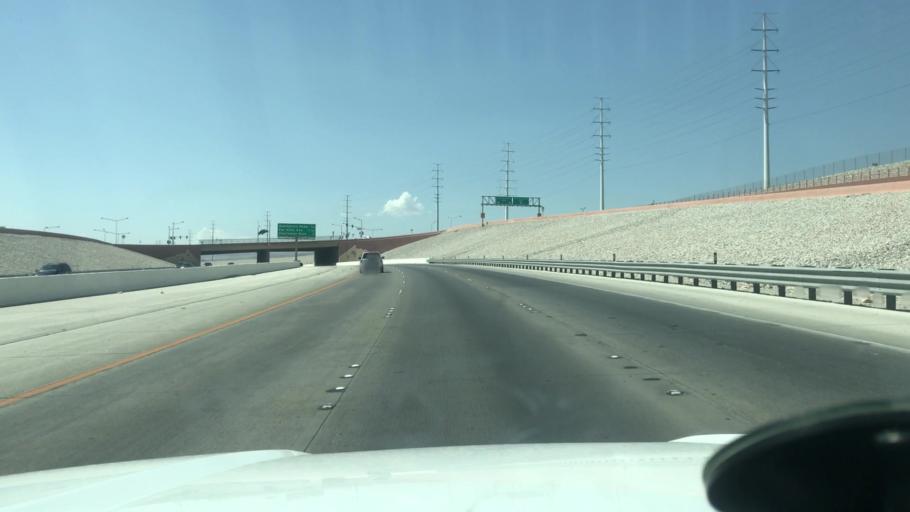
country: US
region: Nevada
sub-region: Clark County
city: Summerlin South
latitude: 36.2088
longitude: -115.3392
